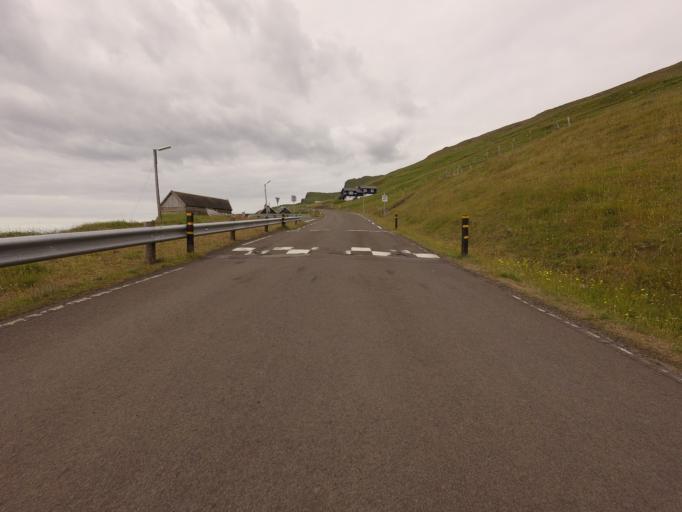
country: FO
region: Suduroy
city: Vagur
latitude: 61.4063
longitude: -6.7254
